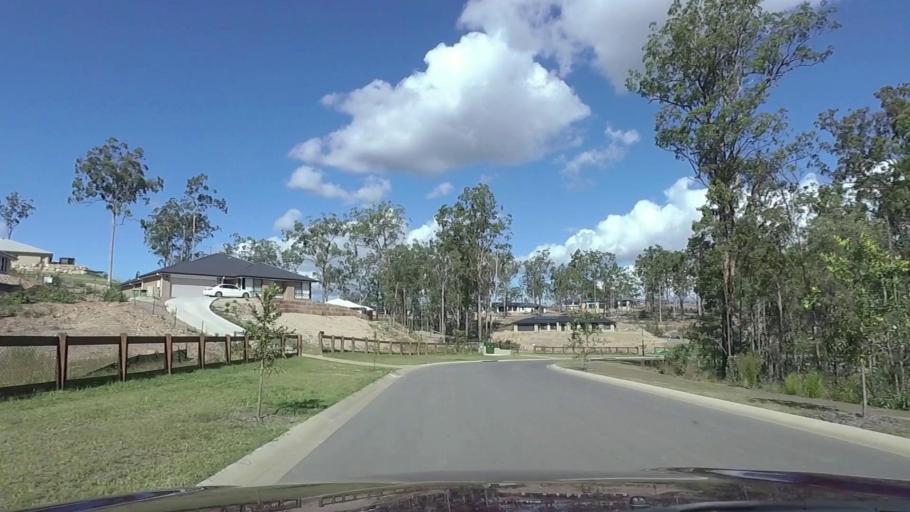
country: AU
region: Queensland
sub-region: Ipswich
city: Springfield Lakes
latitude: -27.7496
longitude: 152.9209
